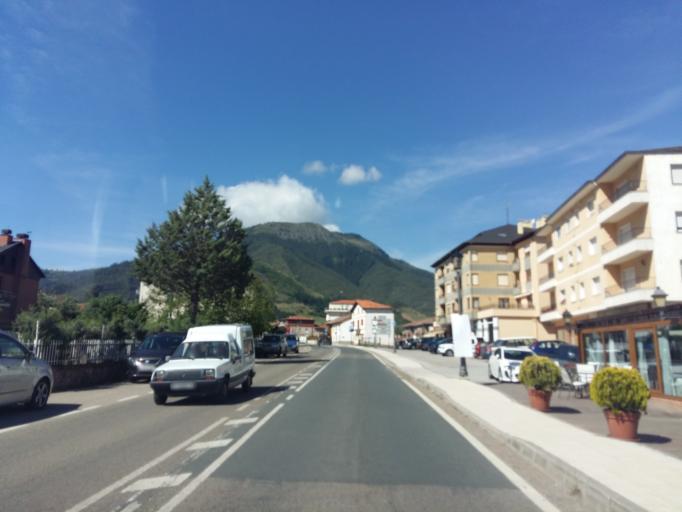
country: ES
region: Cantabria
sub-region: Provincia de Cantabria
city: Potes
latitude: 43.1568
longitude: -4.6176
